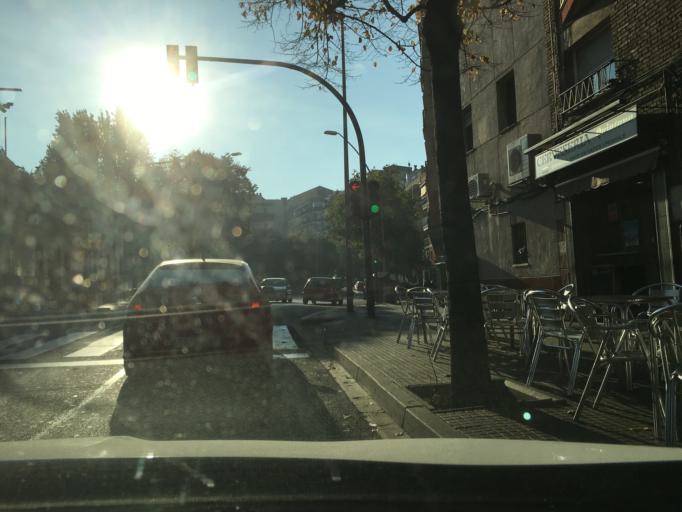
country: ES
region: Catalonia
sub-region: Provincia de Barcelona
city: Santa Coloma de Gramenet
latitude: 41.4565
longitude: 2.2091
